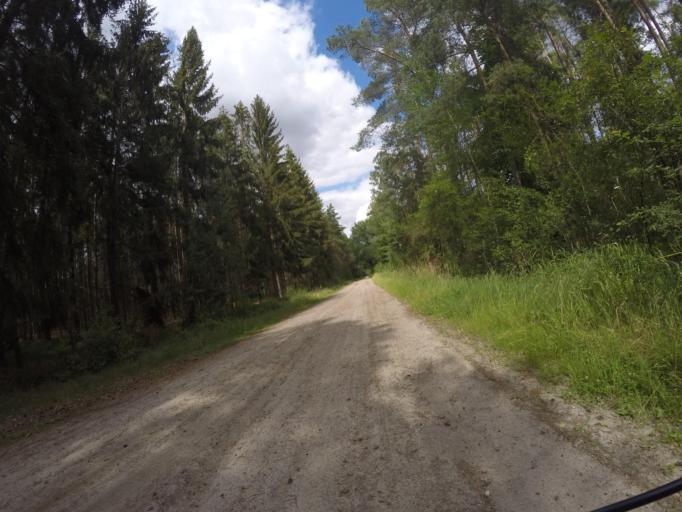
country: DE
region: Lower Saxony
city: Neu Darchau
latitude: 53.2648
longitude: 10.9828
